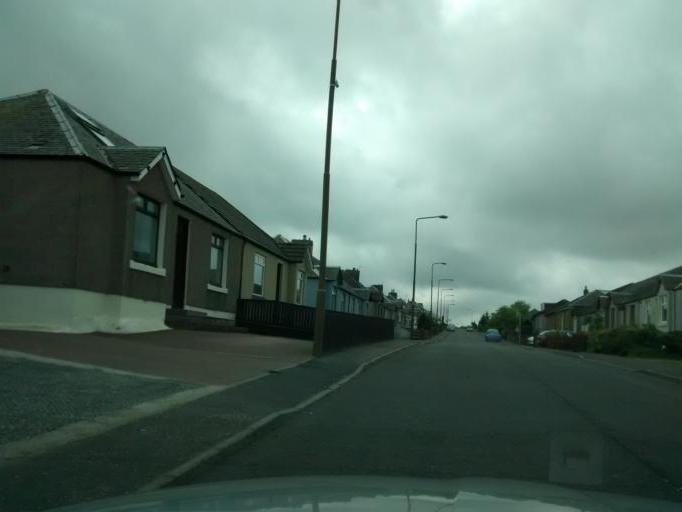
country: GB
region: Scotland
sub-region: North Lanarkshire
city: Harthill
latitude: 55.8802
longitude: -3.7599
